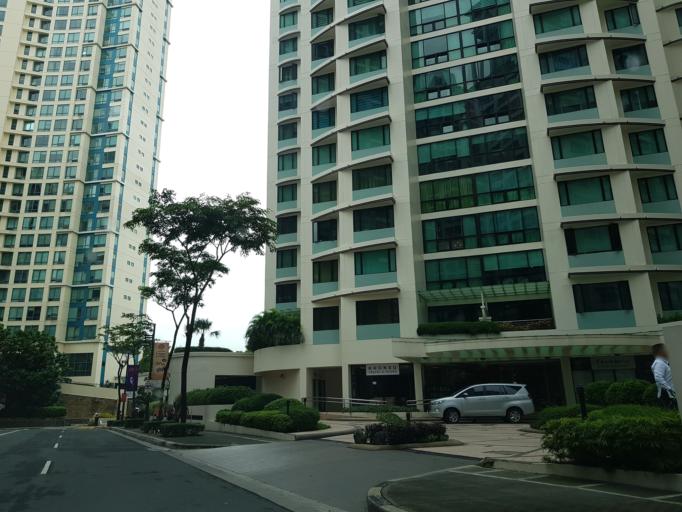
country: PH
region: Metro Manila
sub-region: Makati City
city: Makati City
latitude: 14.5539
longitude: 121.0437
